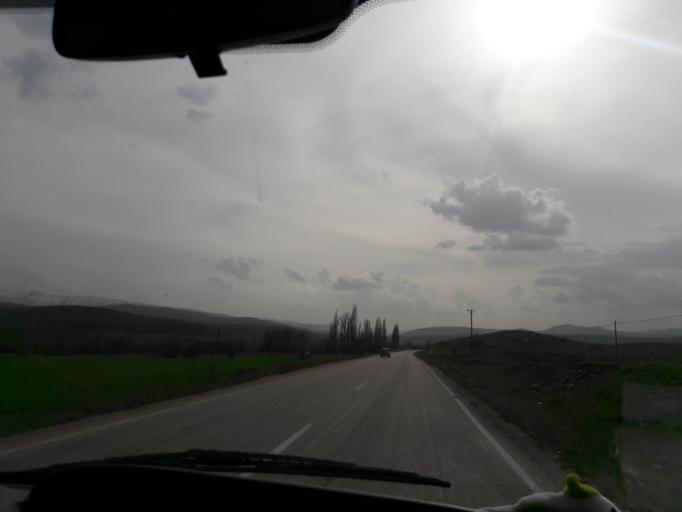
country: TR
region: Gumushane
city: Siran
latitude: 40.1646
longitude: 39.0480
